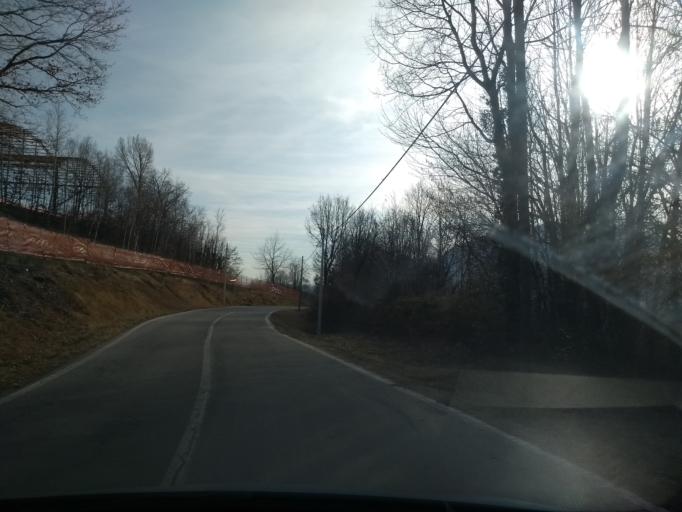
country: IT
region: Piedmont
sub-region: Provincia di Torino
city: Balangero
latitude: 45.2880
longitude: 7.5044
